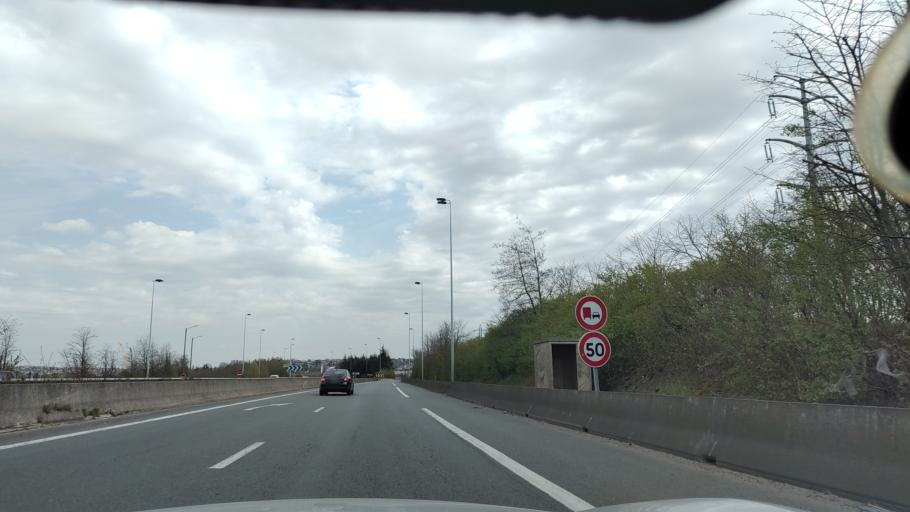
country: FR
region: Ile-de-France
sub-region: Departement du Val-de-Marne
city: Bonneuil-sur-Marne
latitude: 48.7607
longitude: 2.4901
